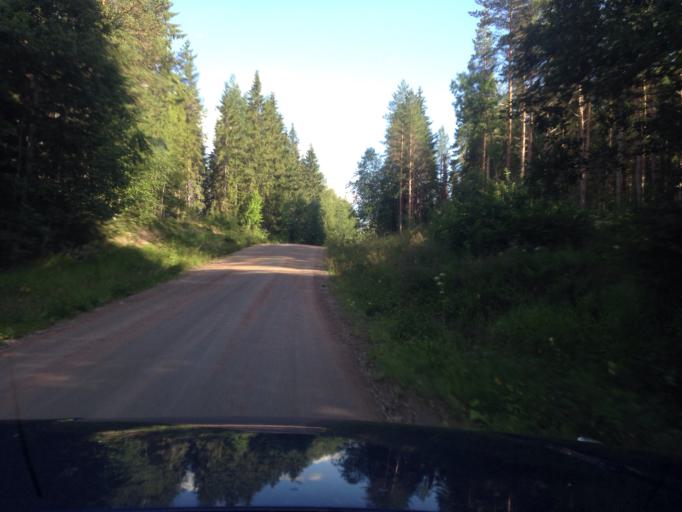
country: SE
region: Dalarna
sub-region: Ludvika Kommun
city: Abborrberget
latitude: 60.2871
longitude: 14.7172
